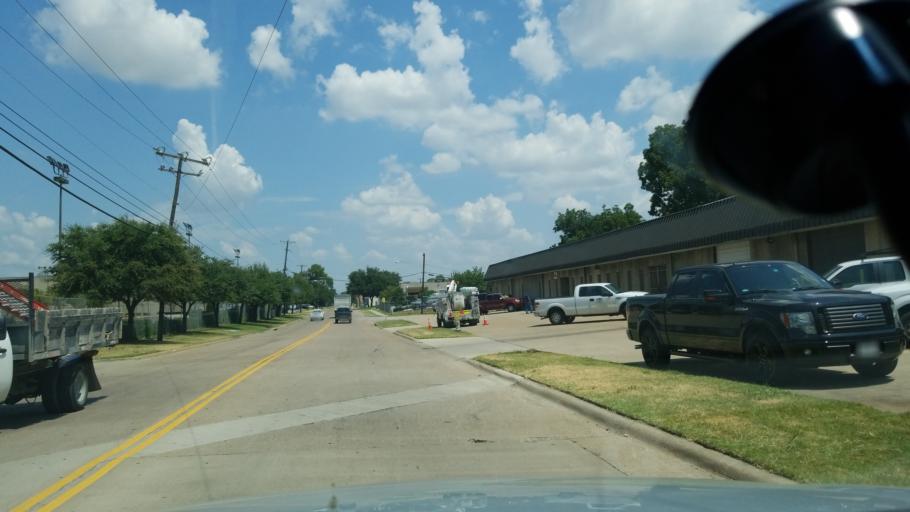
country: US
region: Texas
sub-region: Dallas County
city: Farmers Branch
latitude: 32.8676
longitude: -96.8905
